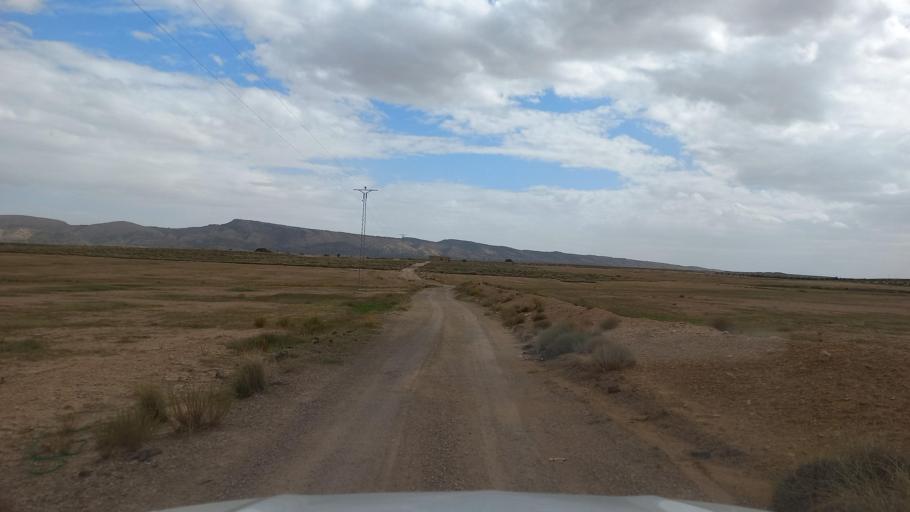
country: TN
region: Al Qasrayn
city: Sbiba
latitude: 35.3845
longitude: 9.1128
